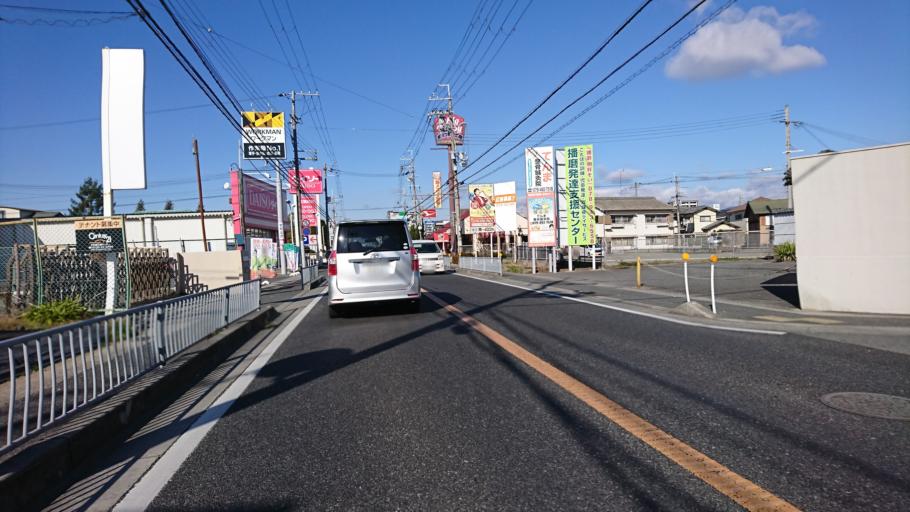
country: JP
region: Hyogo
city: Kakogawacho-honmachi
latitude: 34.7399
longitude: 134.8711
